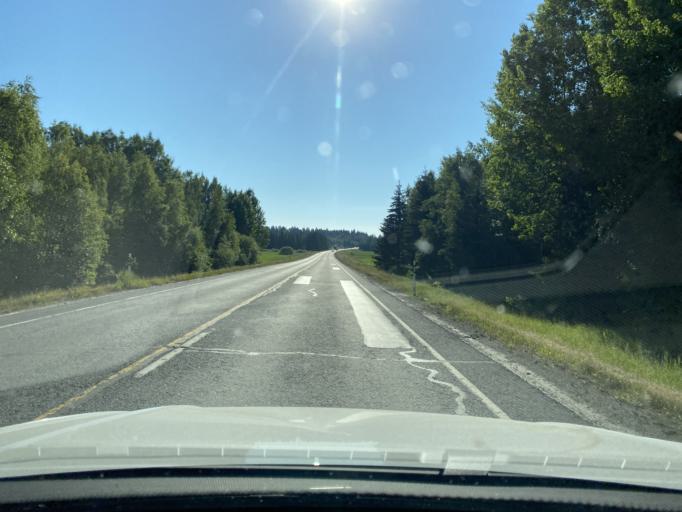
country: FI
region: Haeme
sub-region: Forssa
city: Tammela
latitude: 60.8304
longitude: 23.7024
